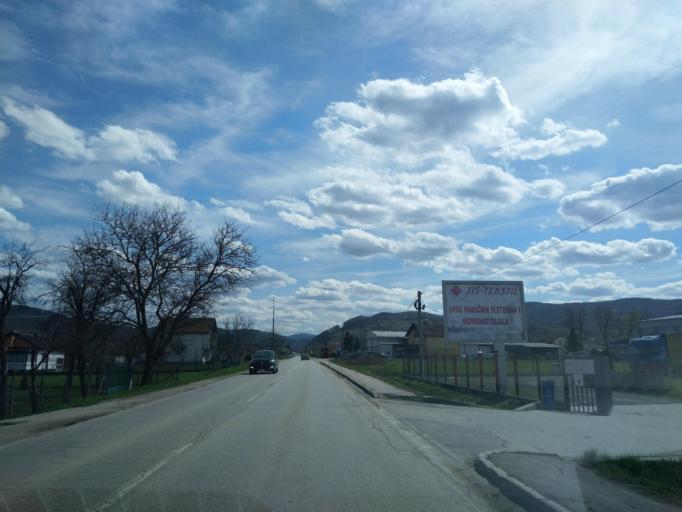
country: RS
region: Central Serbia
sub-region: Zlatiborski Okrug
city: Arilje
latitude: 43.7150
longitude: 20.1157
